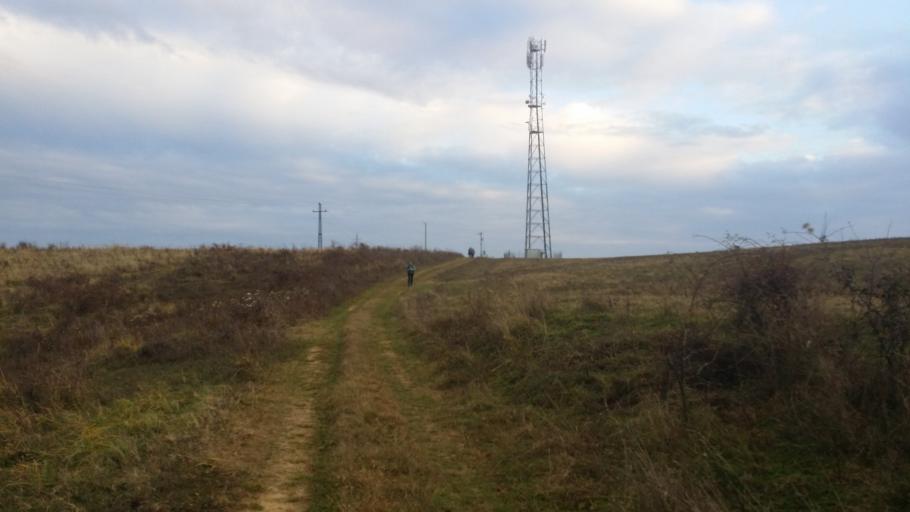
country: HU
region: Tolna
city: Bataszek
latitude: 46.2245
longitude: 18.6207
